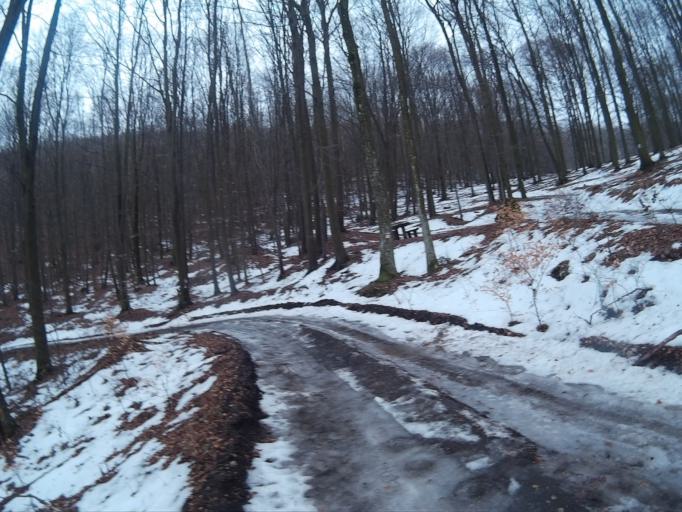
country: HU
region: Heves
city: Belapatfalva
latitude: 48.0466
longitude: 20.3938
